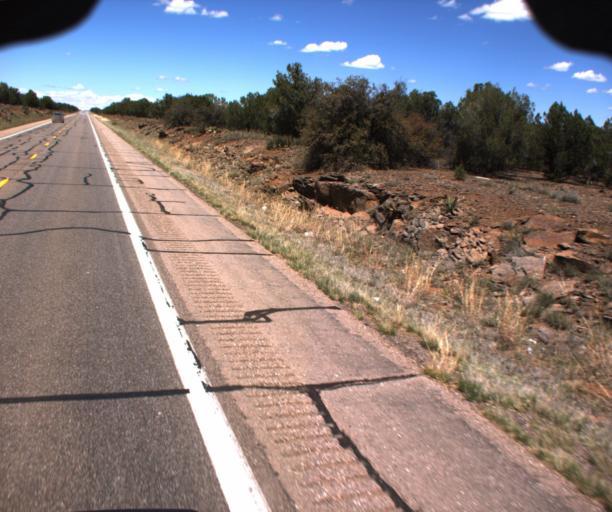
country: US
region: Arizona
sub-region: Yavapai County
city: Paulden
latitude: 35.0215
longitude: -112.3927
